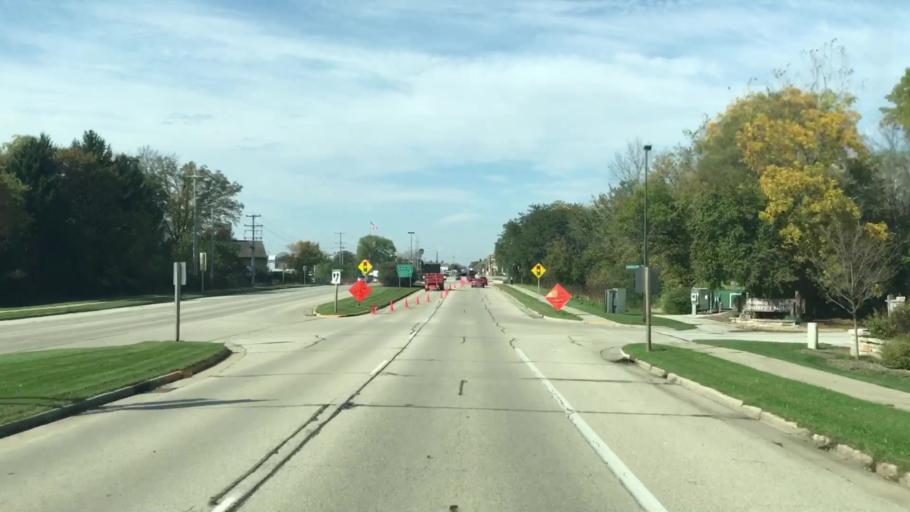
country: US
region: Wisconsin
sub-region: Ozaukee County
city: Thiensville
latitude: 43.2217
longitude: -87.9786
